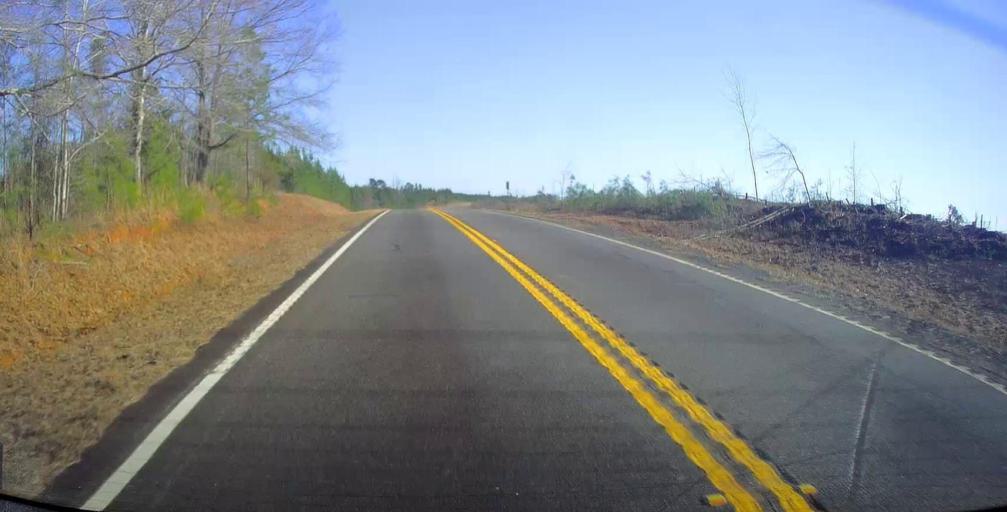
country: US
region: Georgia
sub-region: Talbot County
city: Talbotton
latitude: 32.6646
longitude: -84.4631
